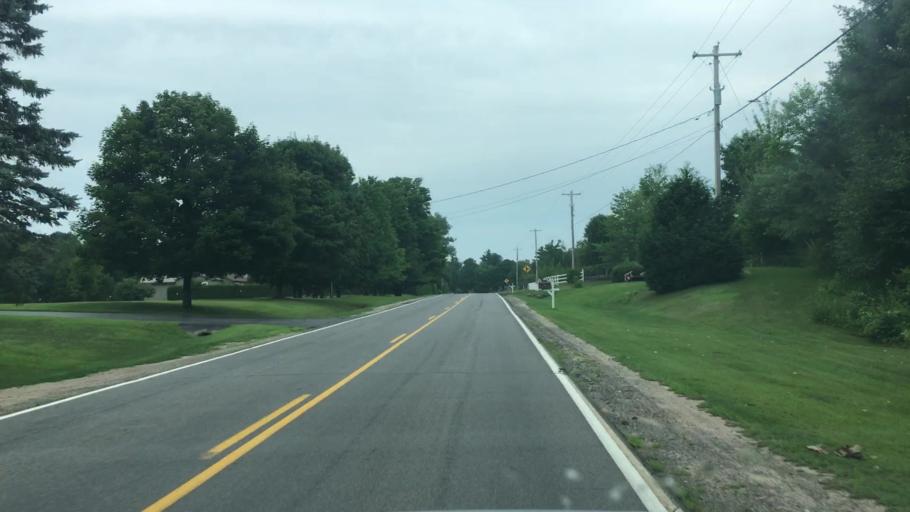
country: US
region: New York
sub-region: Clinton County
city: Morrisonville
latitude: 44.6108
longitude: -73.6346
